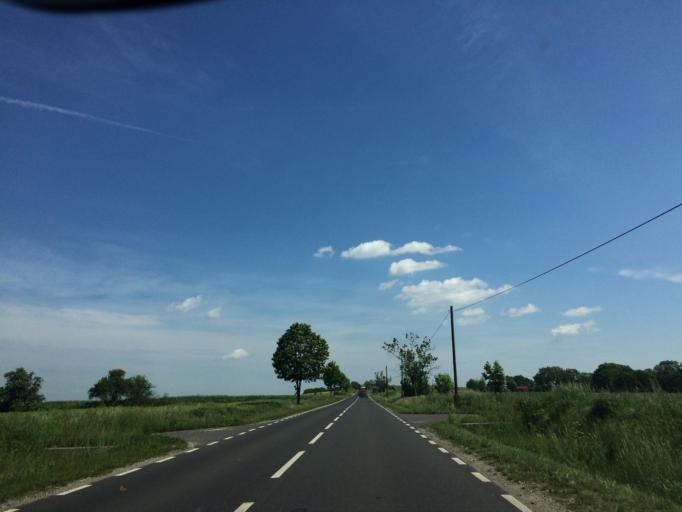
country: PL
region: Lower Silesian Voivodeship
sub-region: Powiat swidnicki
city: Swidnica
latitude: 50.8151
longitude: 16.4949
